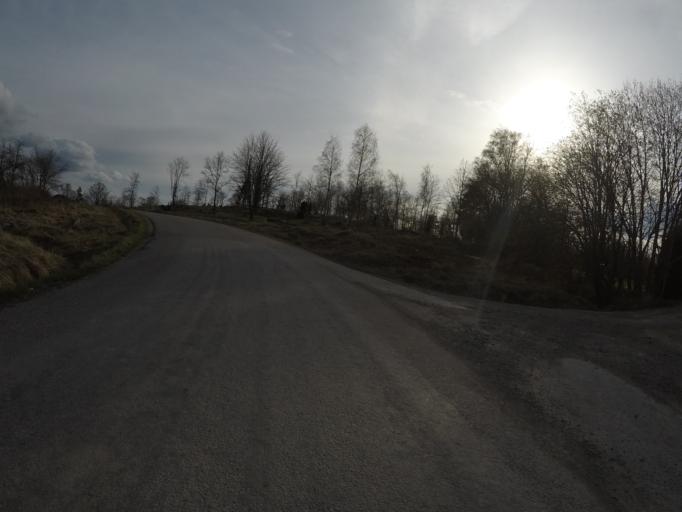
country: SE
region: Soedermanland
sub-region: Eskilstuna Kommun
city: Eskilstuna
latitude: 59.4325
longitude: 16.5474
